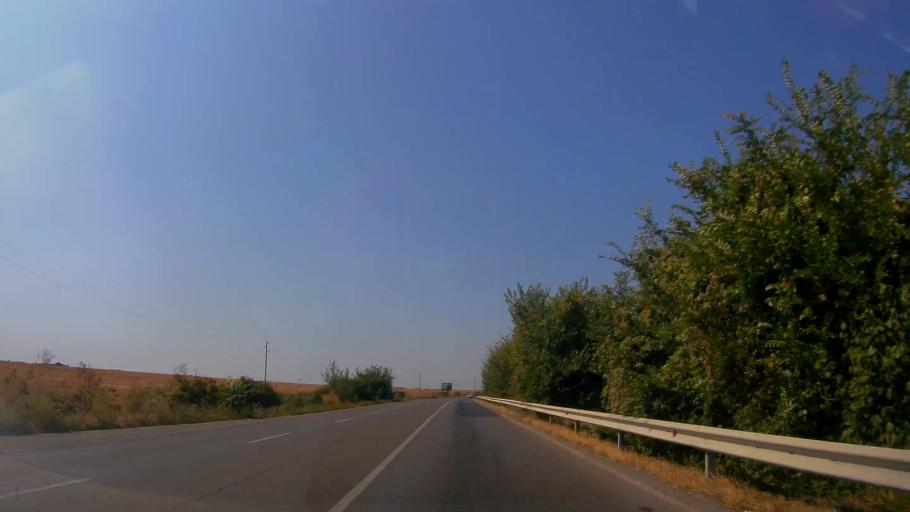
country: BG
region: Ruse
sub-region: Obshtina Vetovo
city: Senovo
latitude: 43.5622
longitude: 26.3473
